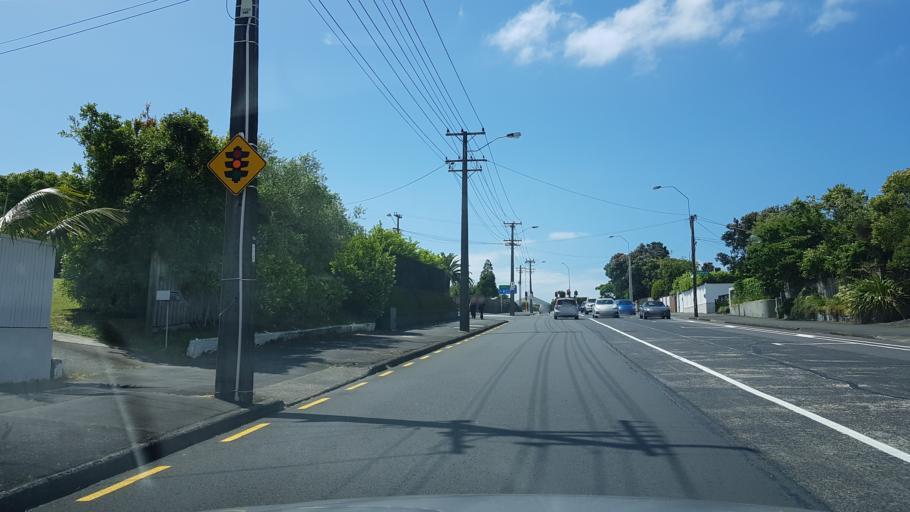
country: NZ
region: Auckland
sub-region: Auckland
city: North Shore
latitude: -36.8131
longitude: 174.7448
